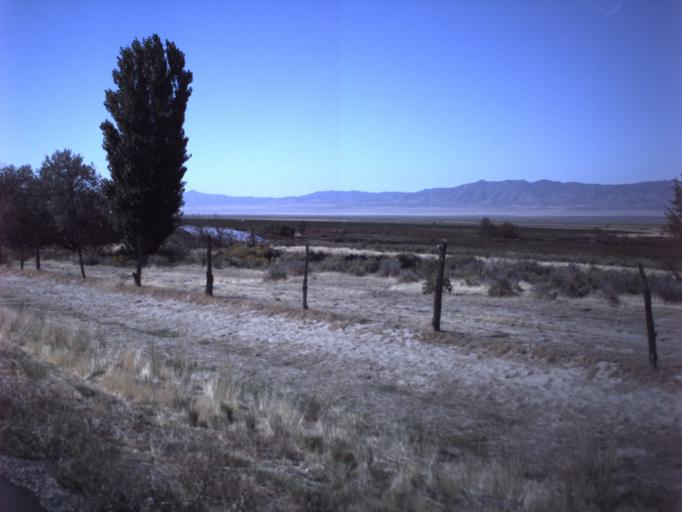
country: US
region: Utah
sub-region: Tooele County
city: Grantsville
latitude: 40.5397
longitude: -112.7458
